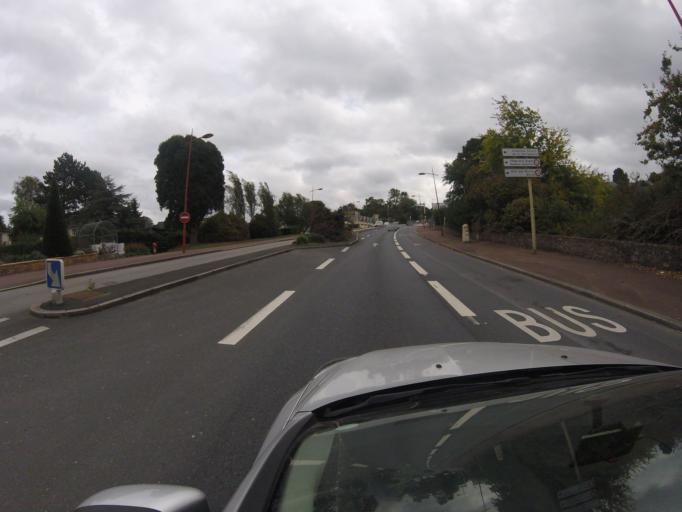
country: FR
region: Lower Normandy
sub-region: Departement de la Manche
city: La Glacerie
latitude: 49.6130
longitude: -1.6016
